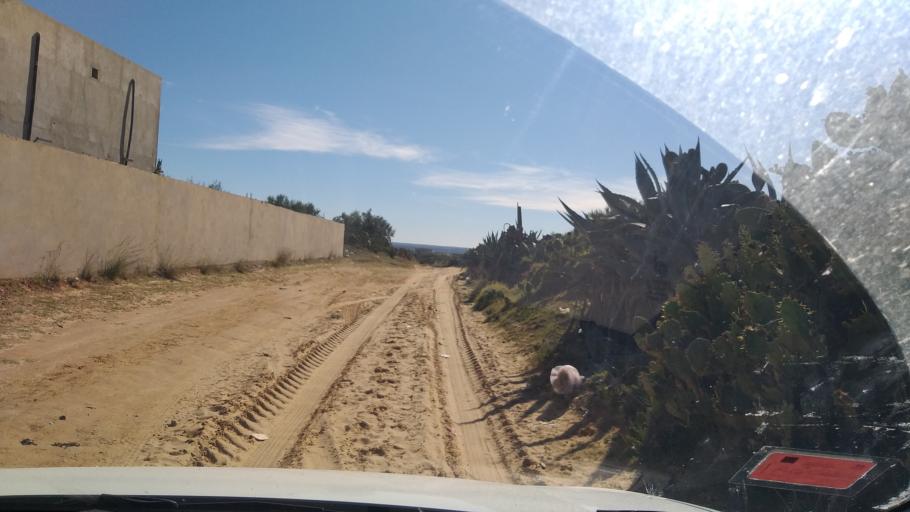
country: TN
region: Al Mahdiyah
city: El Jem
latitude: 35.2579
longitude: 10.6051
